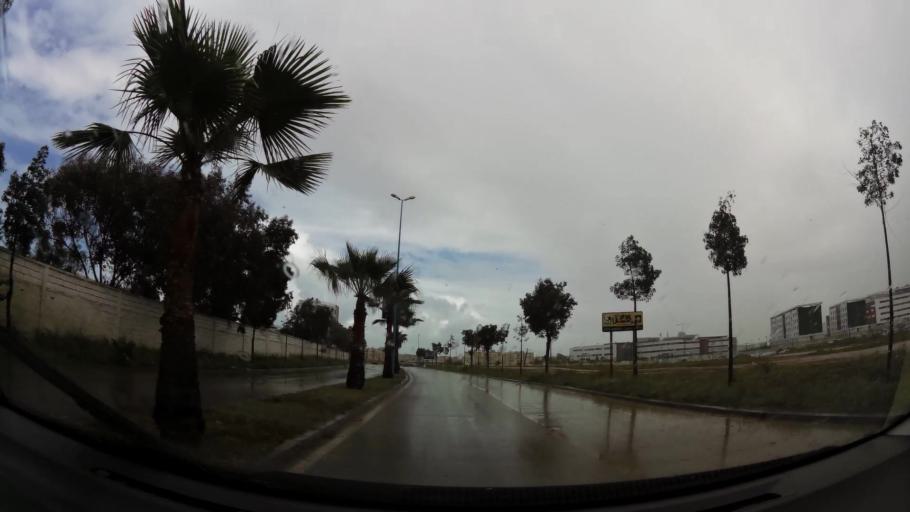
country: MA
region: Grand Casablanca
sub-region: Casablanca
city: Casablanca
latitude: 33.5491
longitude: -7.6700
